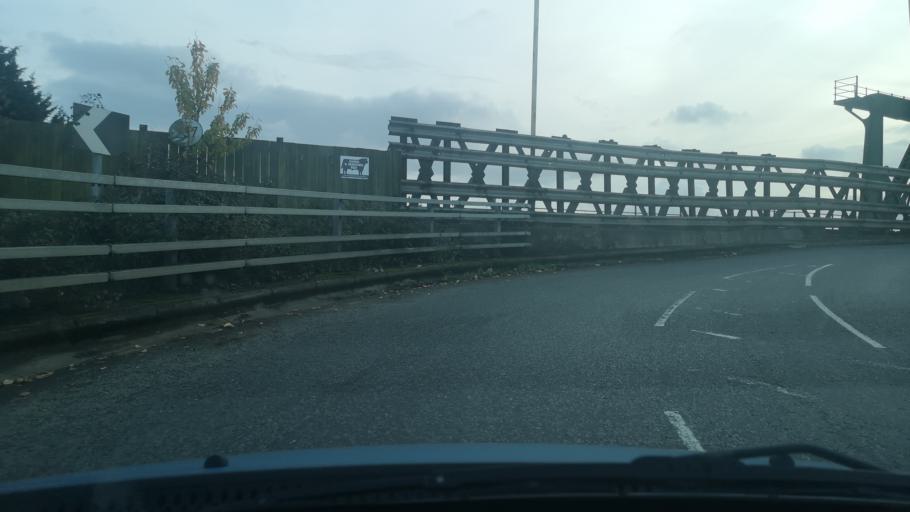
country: GB
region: England
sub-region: North Lincolnshire
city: Gunness
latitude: 53.5860
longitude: -0.7292
